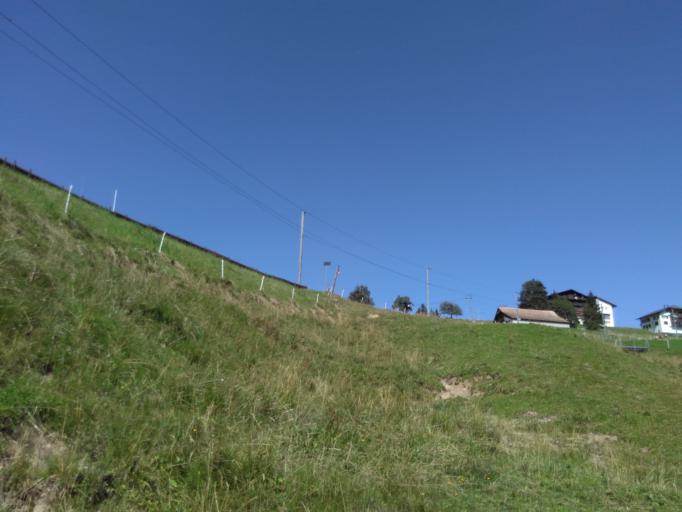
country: CH
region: Lucerne
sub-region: Lucerne-Land District
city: Vitznau
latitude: 47.0495
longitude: 8.4725
